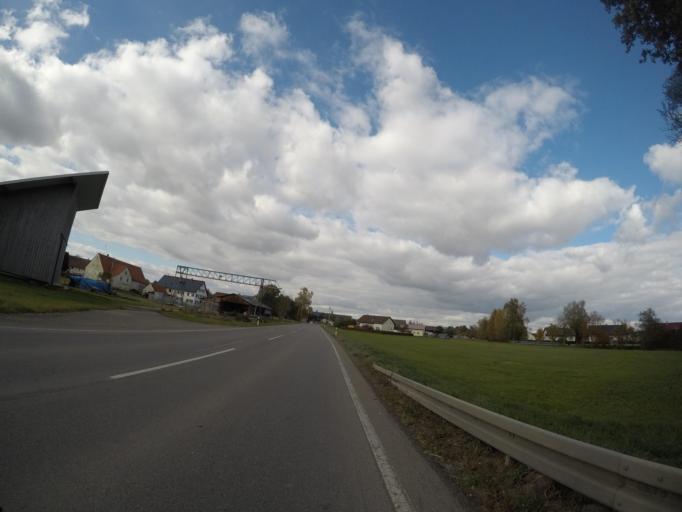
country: DE
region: Baden-Wuerttemberg
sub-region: Tuebingen Region
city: Unterstadion
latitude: 48.2036
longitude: 9.6827
